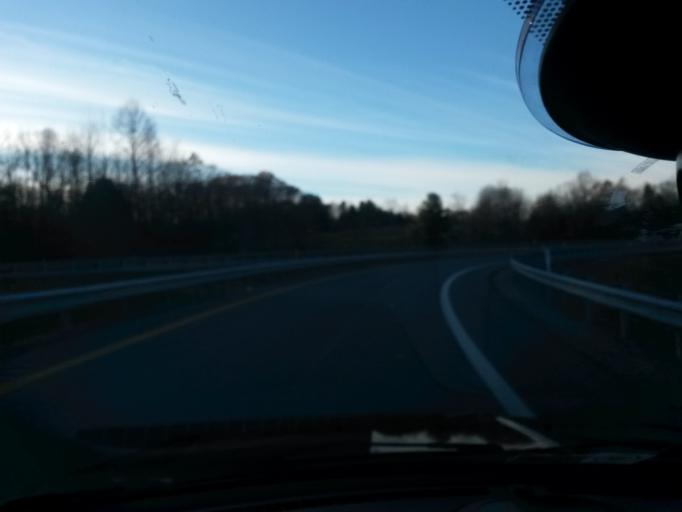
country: US
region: West Virginia
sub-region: Raleigh County
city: Prosperity
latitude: 37.8317
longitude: -81.2155
